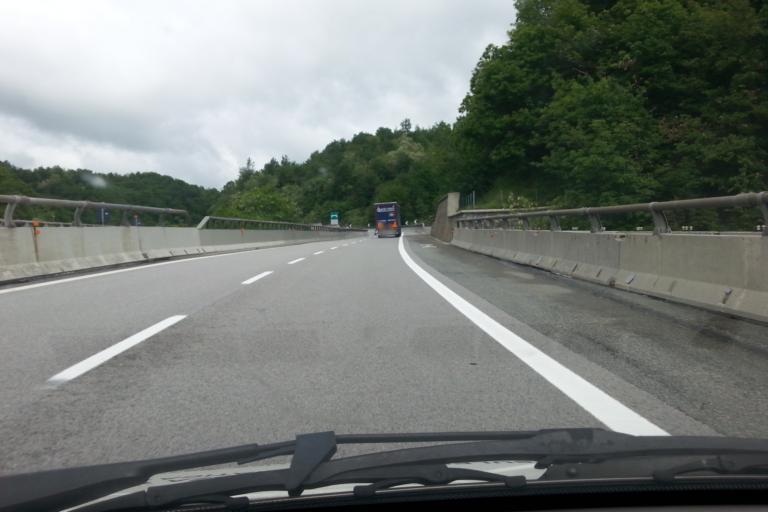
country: IT
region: Liguria
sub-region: Provincia di Savona
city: Valzemola
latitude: 44.3595
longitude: 8.1643
